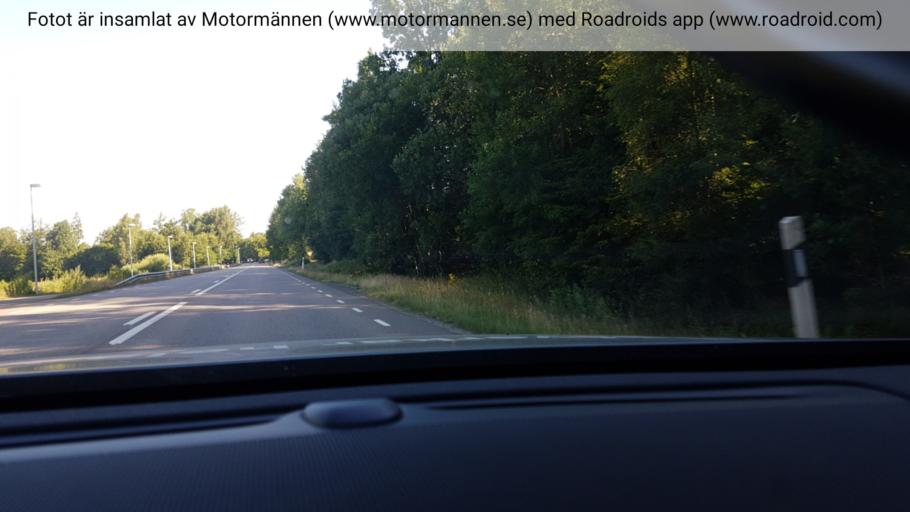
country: SE
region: Skane
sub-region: Hassleholms Kommun
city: Bjarnum
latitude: 56.3233
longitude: 13.6840
